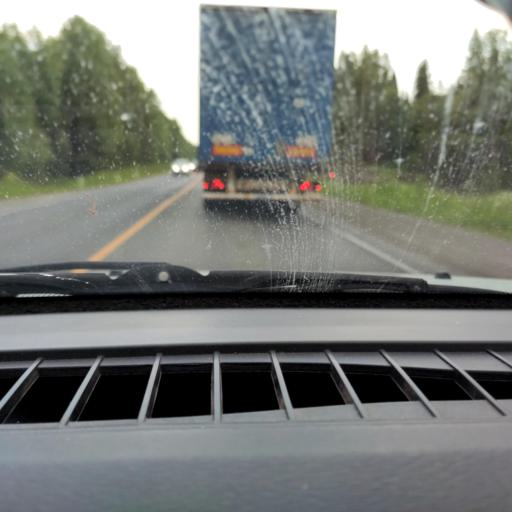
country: RU
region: Perm
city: Kukushtan
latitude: 57.5613
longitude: 56.5723
